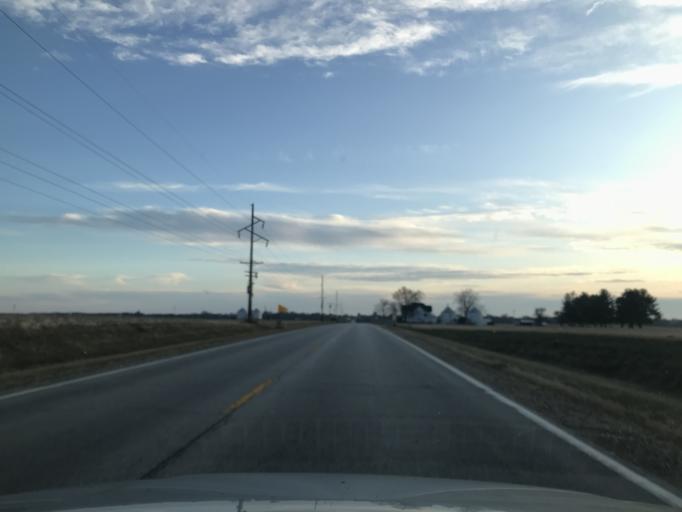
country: US
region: Illinois
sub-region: Warren County
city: Monmouth
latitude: 41.0276
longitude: -90.7463
